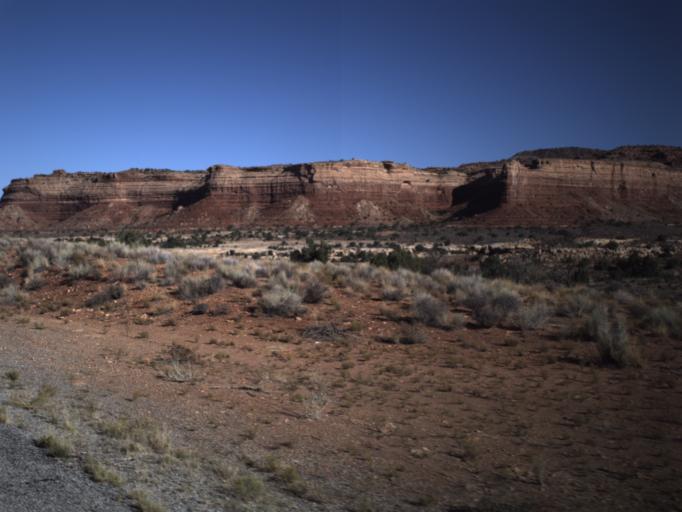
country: US
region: Utah
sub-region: San Juan County
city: Blanding
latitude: 37.7329
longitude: -110.2587
